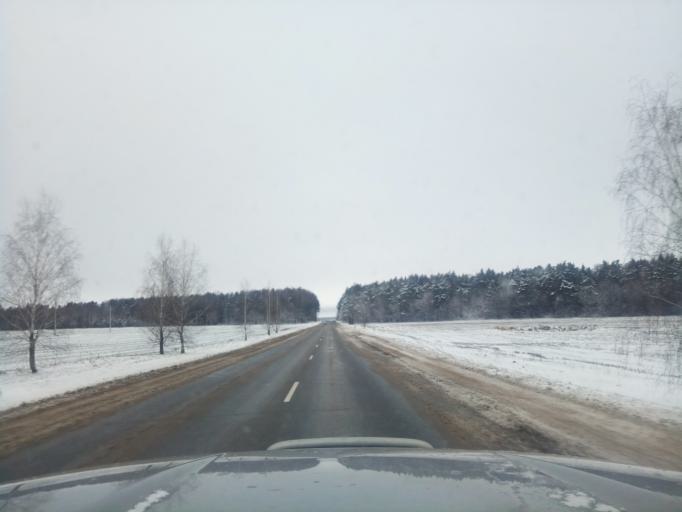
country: BY
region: Minsk
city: Kapyl'
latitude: 53.1556
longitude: 27.1133
